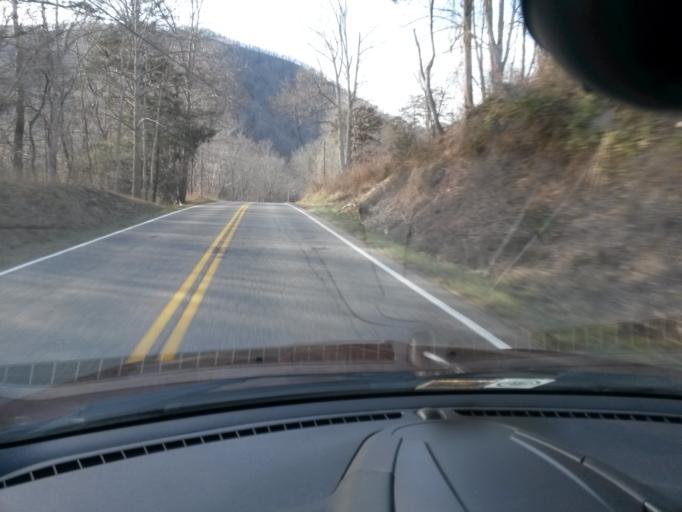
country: US
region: Virginia
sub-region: Rockbridge County
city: East Lexington
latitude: 38.0014
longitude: -79.5273
